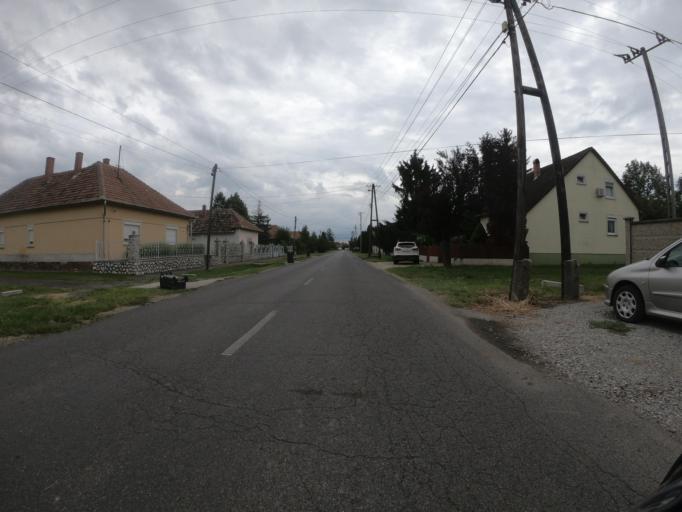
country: HU
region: Borsod-Abauj-Zemplen
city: Szentistvan
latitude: 47.7781
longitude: 20.6516
